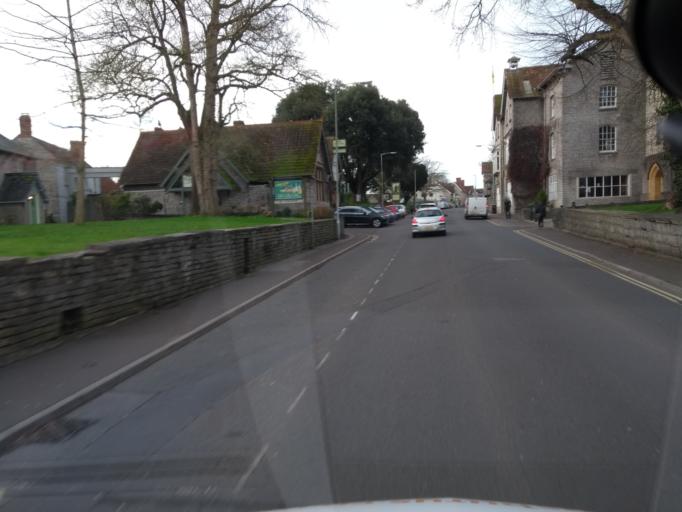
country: GB
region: England
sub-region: Somerset
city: Street
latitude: 51.1287
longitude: -2.7375
